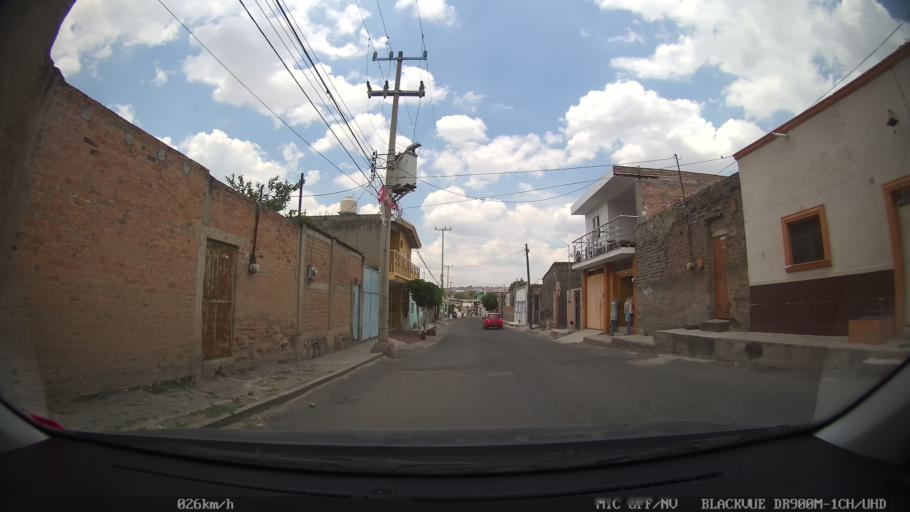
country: MX
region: Jalisco
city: Tonala
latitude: 20.6611
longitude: -103.2264
